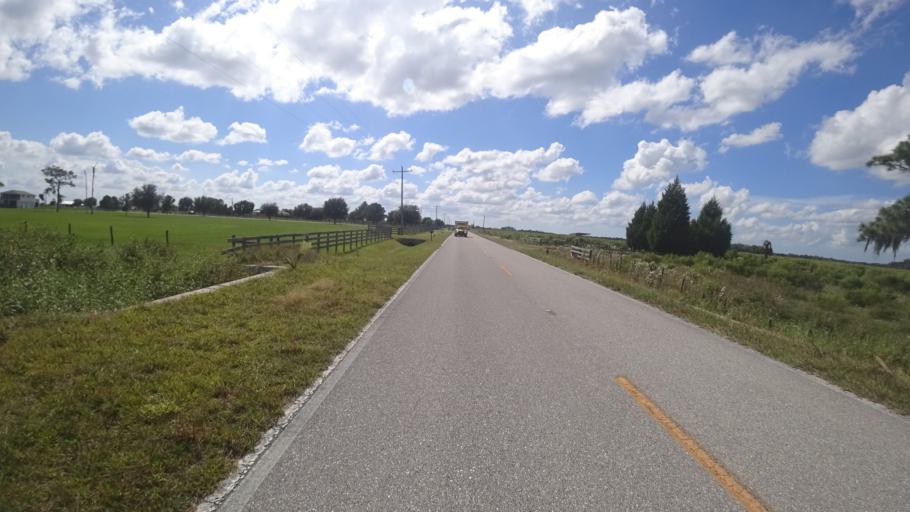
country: US
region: Florida
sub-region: Sarasota County
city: Lake Sarasota
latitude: 27.3058
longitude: -82.1847
